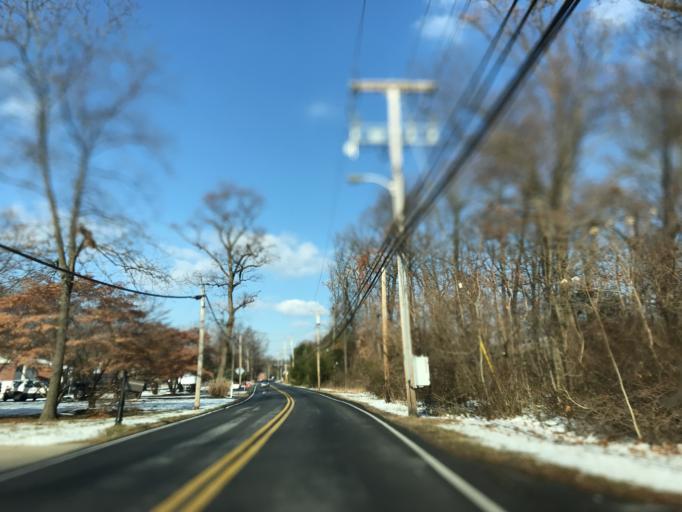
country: US
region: Maryland
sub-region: Baltimore County
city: Bowleys Quarters
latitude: 39.3227
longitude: -76.3926
